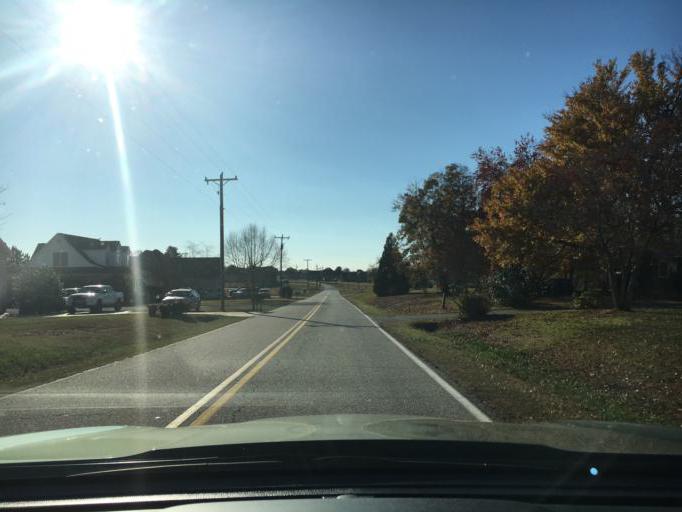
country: US
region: South Carolina
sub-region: Spartanburg County
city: Inman Mills
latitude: 35.0512
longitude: -82.1360
